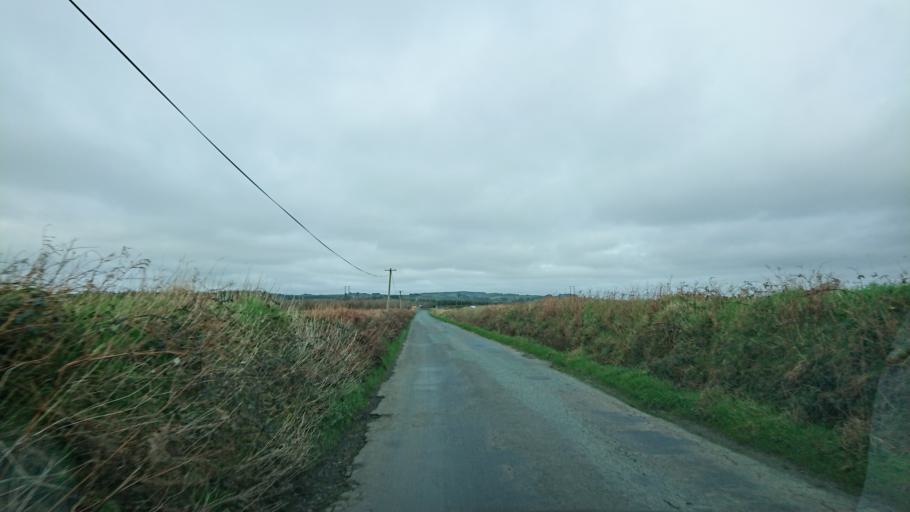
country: IE
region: Munster
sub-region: Waterford
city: Portlaw
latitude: 52.1791
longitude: -7.3029
